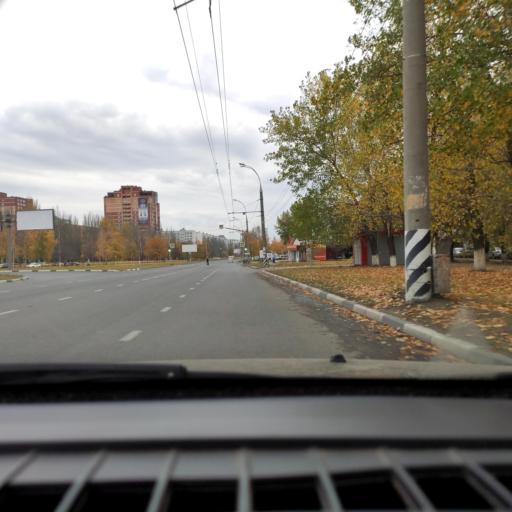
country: RU
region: Samara
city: Tol'yatti
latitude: 53.5176
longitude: 49.2938
